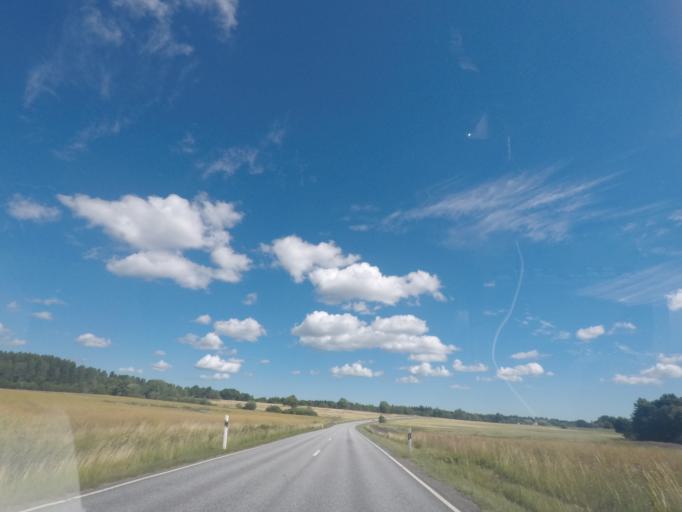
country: SE
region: Stockholm
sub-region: Norrtalje Kommun
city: Hallstavik
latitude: 59.9362
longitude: 18.7206
